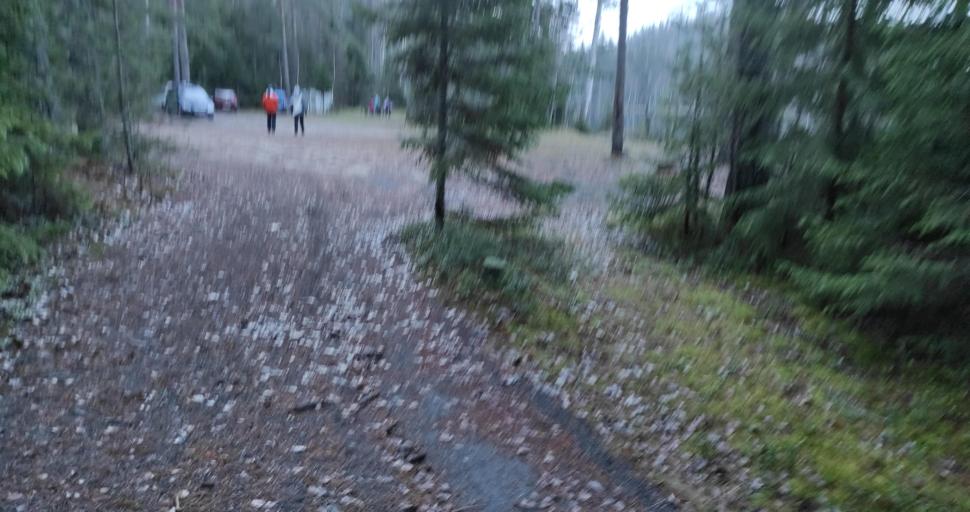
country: RU
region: Republic of Karelia
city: Pitkyaranta
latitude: 61.7556
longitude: 31.3332
